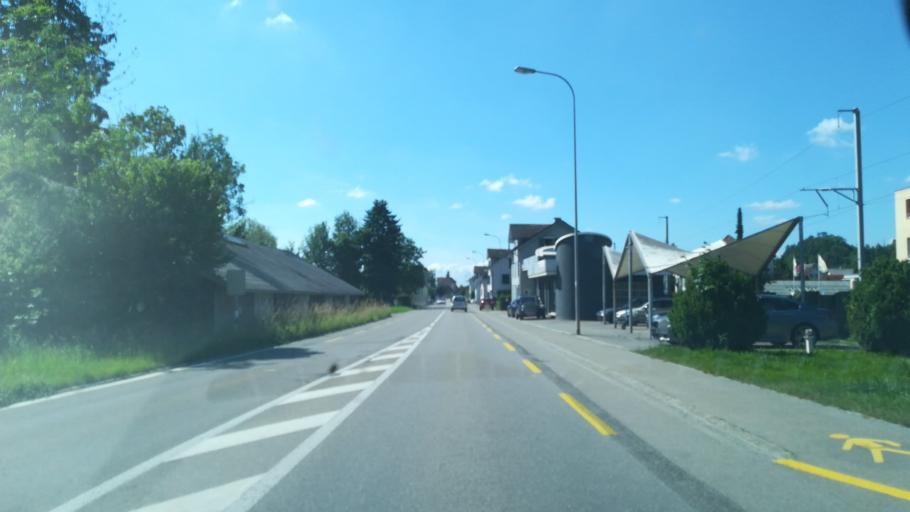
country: CH
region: Thurgau
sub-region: Weinfelden District
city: Sulgen
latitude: 47.5224
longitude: 9.2051
